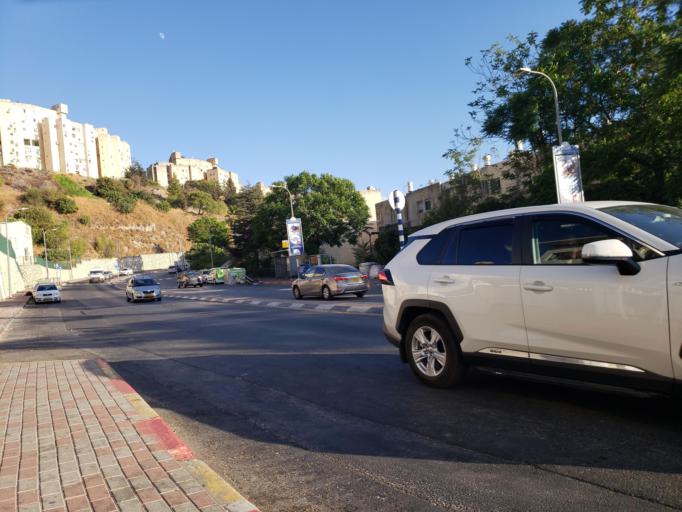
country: IL
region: Northern District
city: Safed
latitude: 32.9637
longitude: 35.4894
